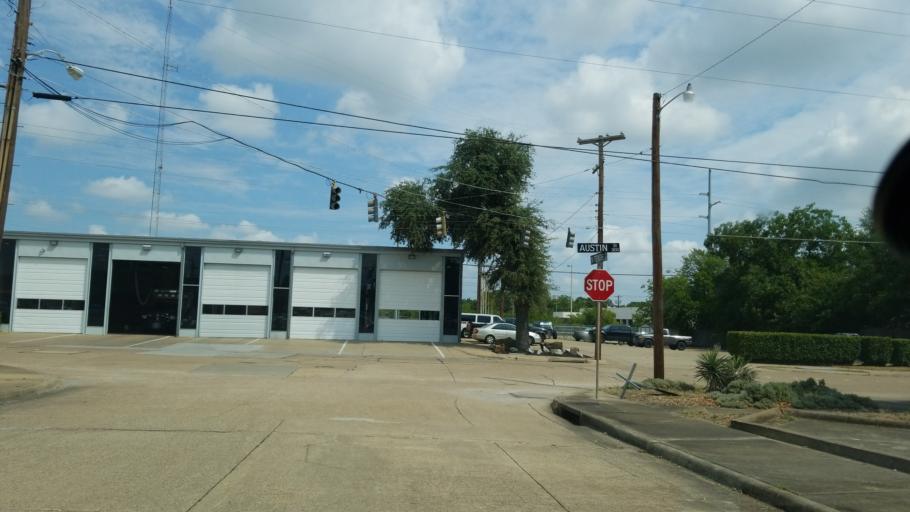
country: US
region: Texas
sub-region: Dallas County
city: Garland
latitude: 32.9142
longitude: -96.6426
